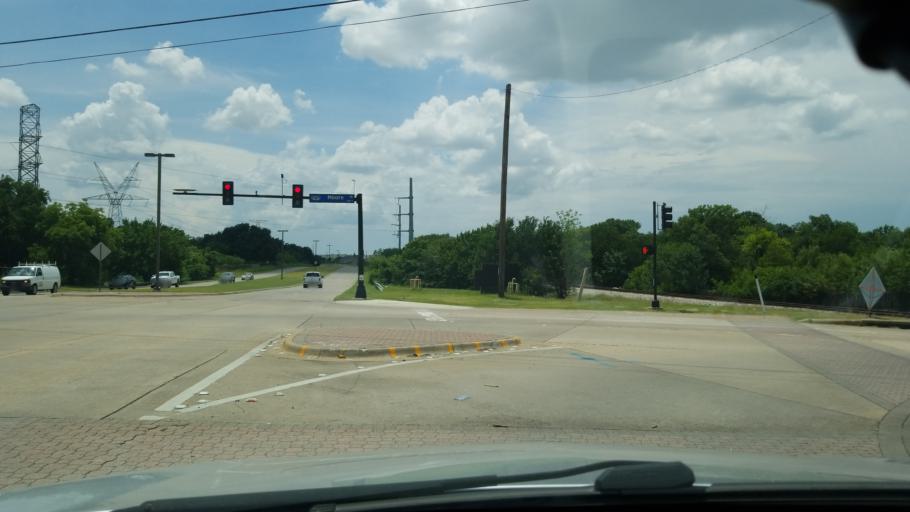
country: US
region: Texas
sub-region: Dallas County
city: Coppell
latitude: 32.9550
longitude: -96.9765
